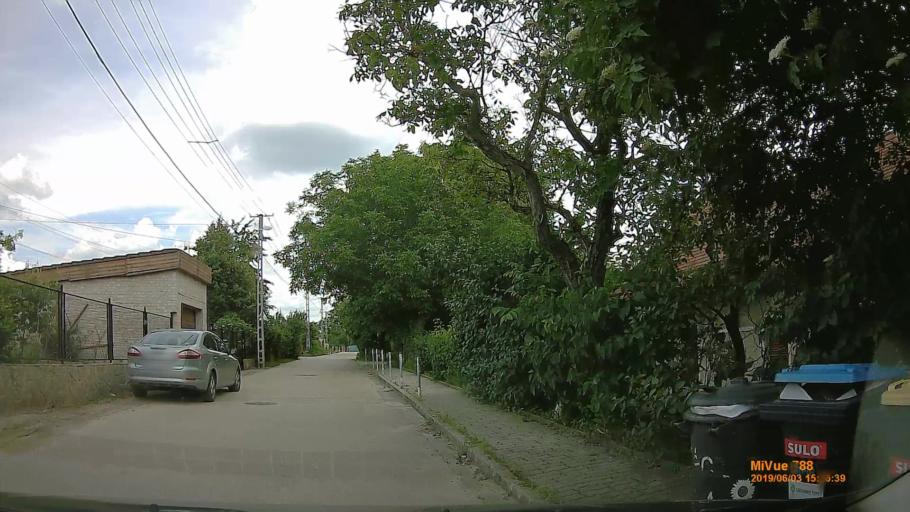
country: HU
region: Budapest
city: Budapest XXII. keruelet
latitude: 47.4317
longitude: 19.0224
